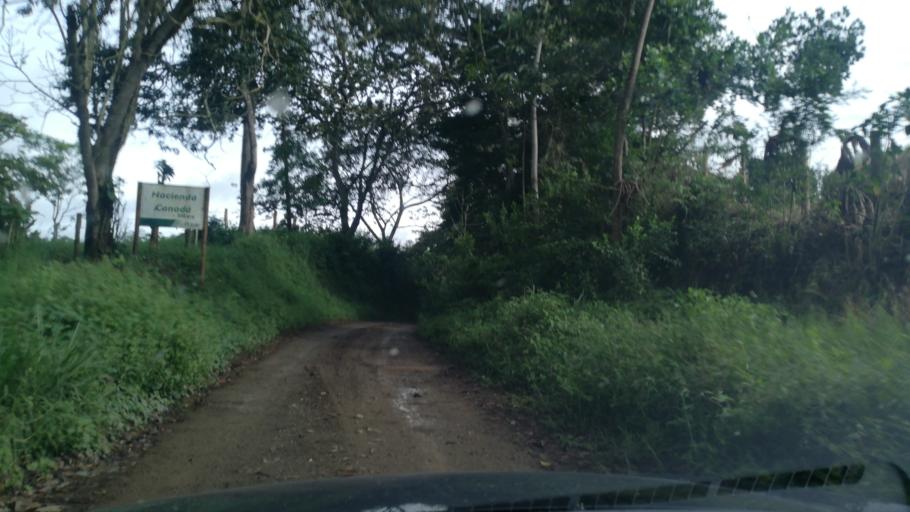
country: CO
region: Valle del Cauca
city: Restrepo
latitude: 3.8528
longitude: -76.4599
